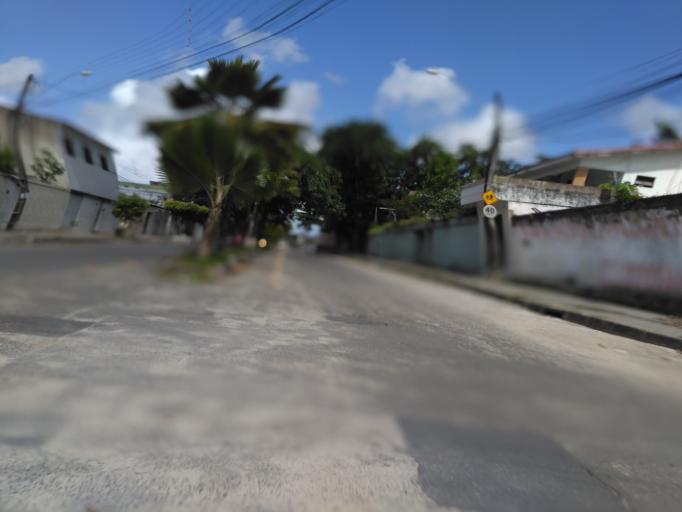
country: BR
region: Pernambuco
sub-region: Recife
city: Recife
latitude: -8.0478
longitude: -34.9359
